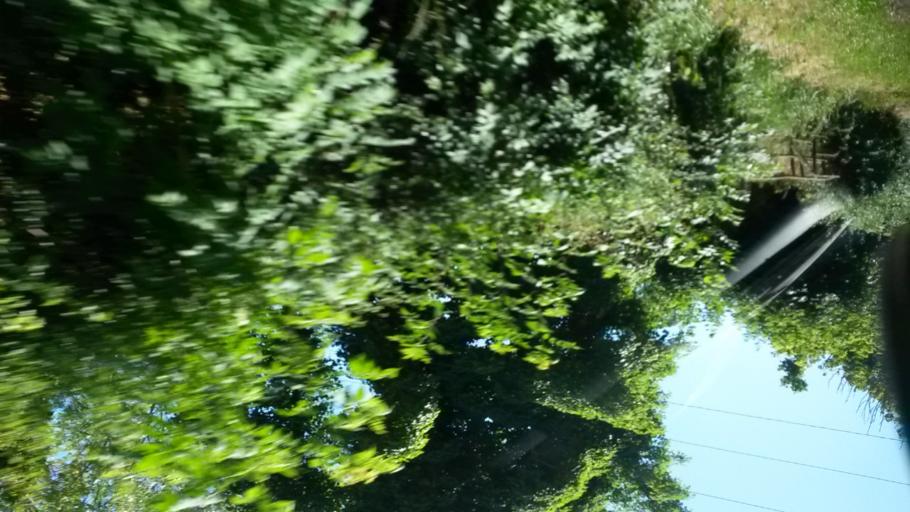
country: IE
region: Leinster
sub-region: Fingal County
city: Swords
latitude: 53.4682
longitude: -6.2726
